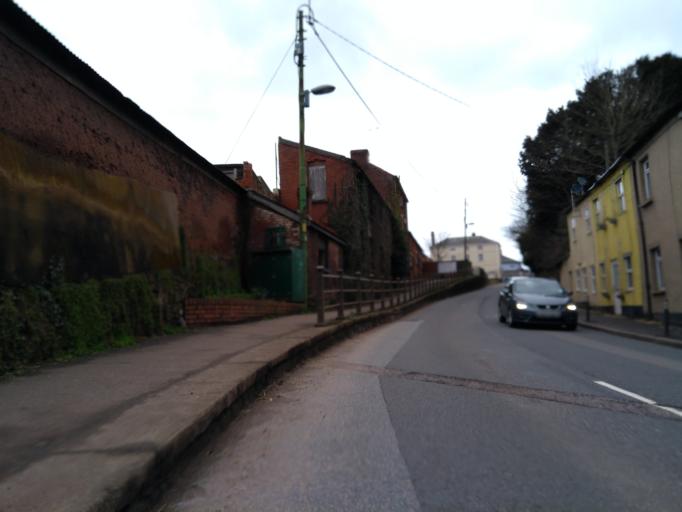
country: GB
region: England
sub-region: Devon
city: Crediton
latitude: 50.7864
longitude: -3.6490
